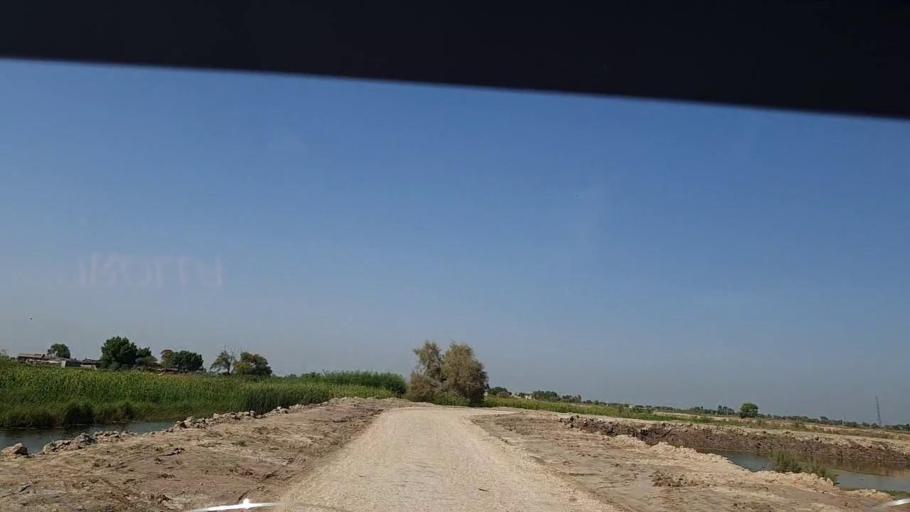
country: PK
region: Sindh
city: Tangwani
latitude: 28.3220
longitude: 69.0831
